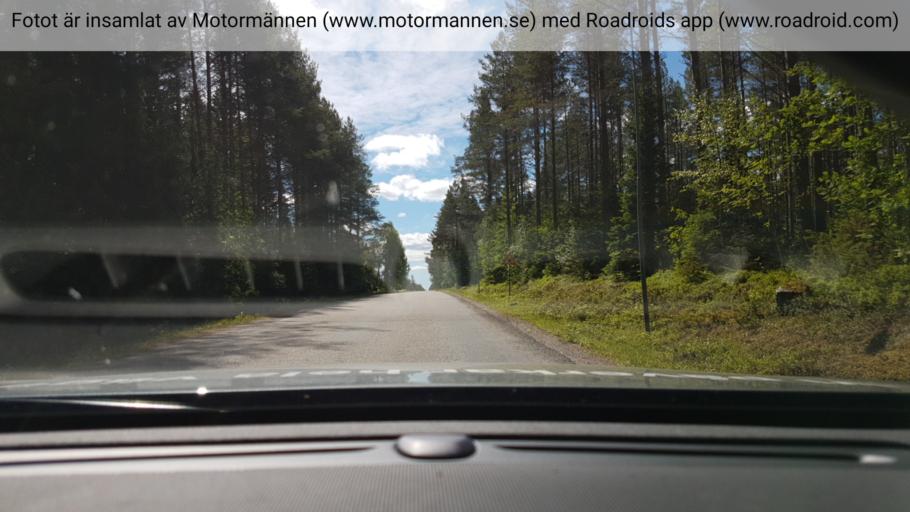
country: SE
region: Vaesterbotten
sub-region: Skelleftea Kommun
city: Burea
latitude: 64.4465
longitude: 21.3550
